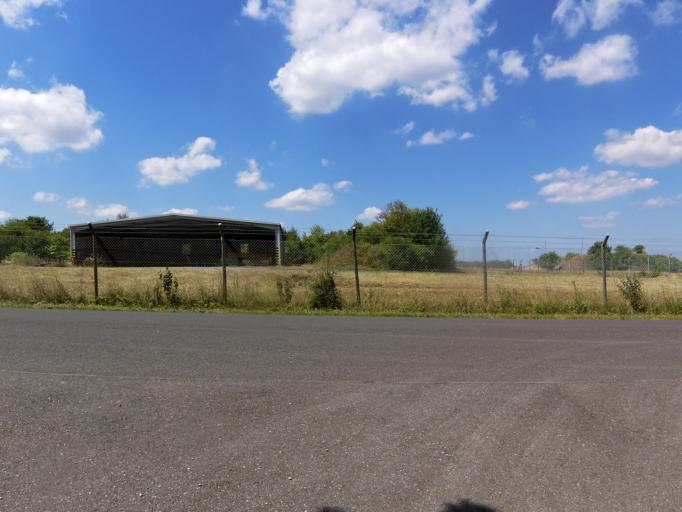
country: DE
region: Bavaria
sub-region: Regierungsbezirk Unterfranken
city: Veitshochheim
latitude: 49.8191
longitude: 9.9026
